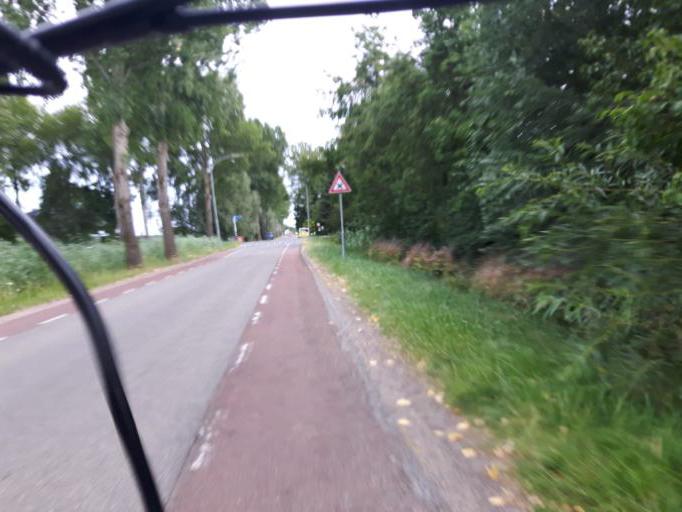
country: NL
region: Gelderland
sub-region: Gemeente Maasdriel
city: Heerewaarden
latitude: 51.8678
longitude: 5.3749
